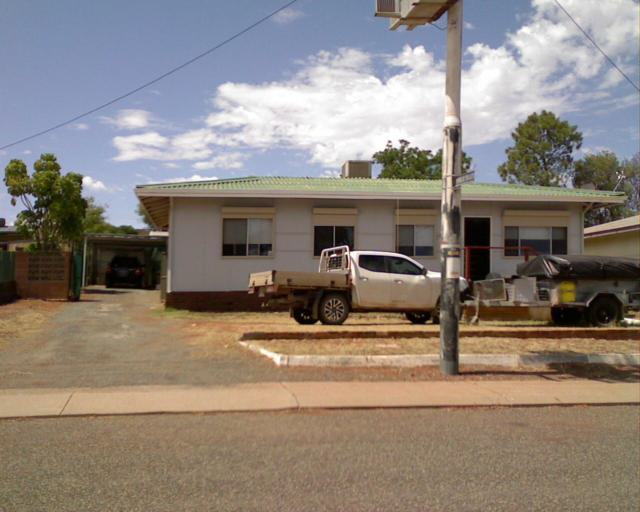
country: AU
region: Western Australia
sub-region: Kalgoorlie/Boulder
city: Stoneville
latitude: -31.2049
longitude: 121.6673
